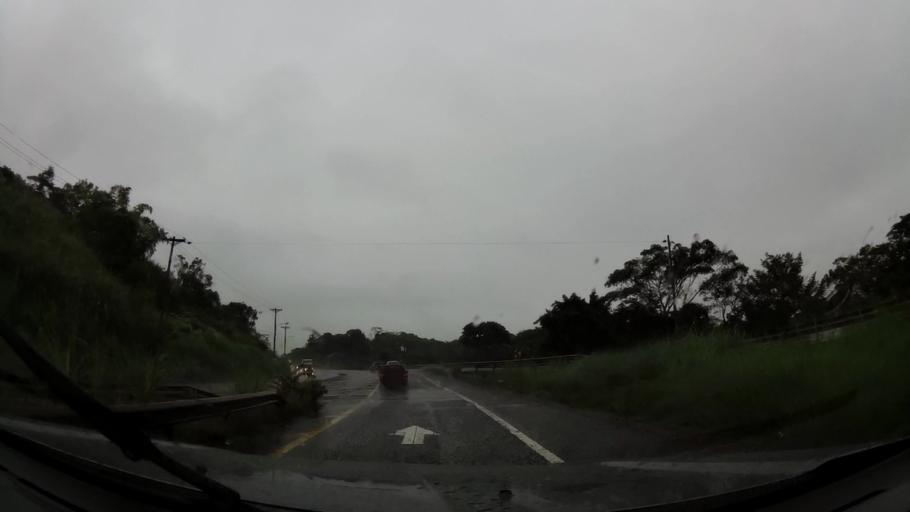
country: PA
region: Colon
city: Santa Rita Arriba
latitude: 9.3252
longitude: -79.7998
